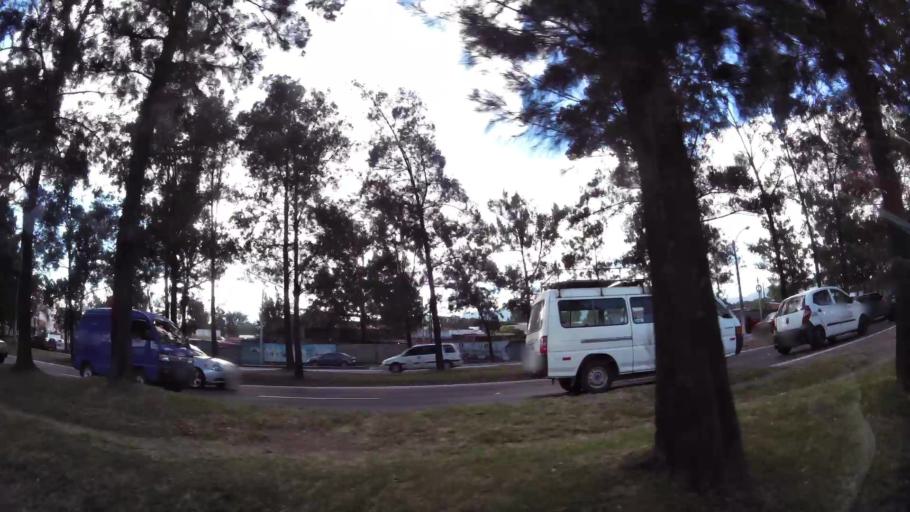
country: GT
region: Guatemala
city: Guatemala City
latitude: 14.6153
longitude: -90.5543
